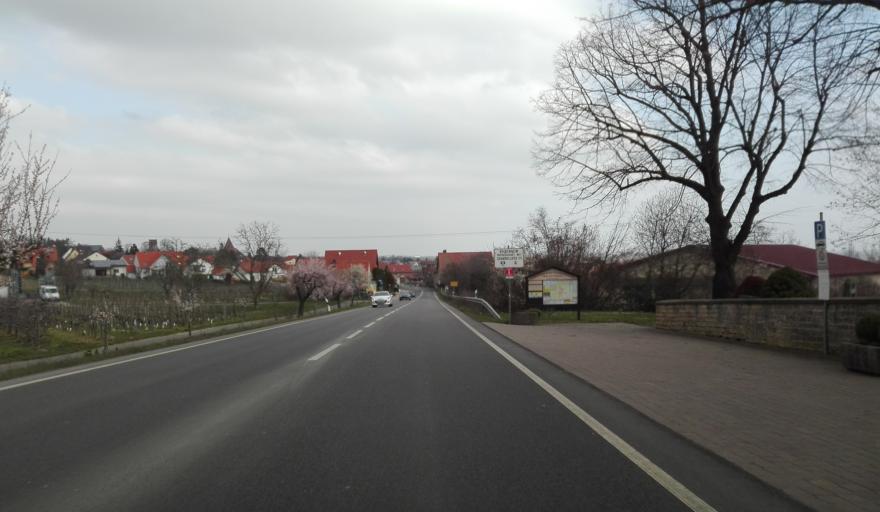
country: DE
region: Rheinland-Pfalz
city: Bockenheim
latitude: 49.5981
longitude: 8.1794
